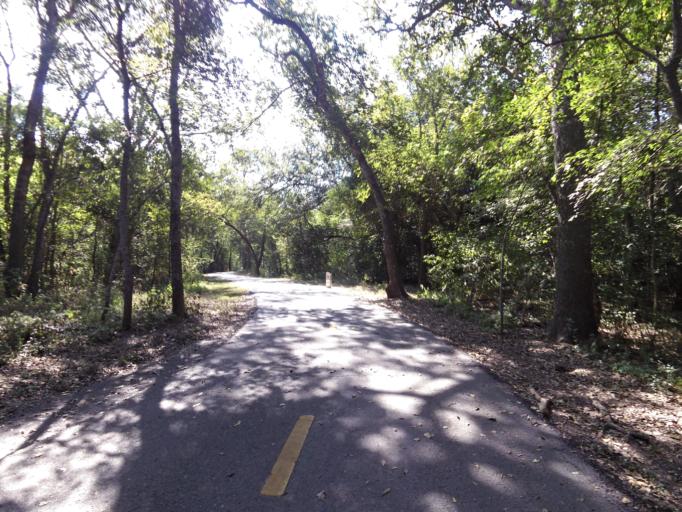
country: US
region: Texas
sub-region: Bexar County
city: Kirby
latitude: 29.4449
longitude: -98.4214
